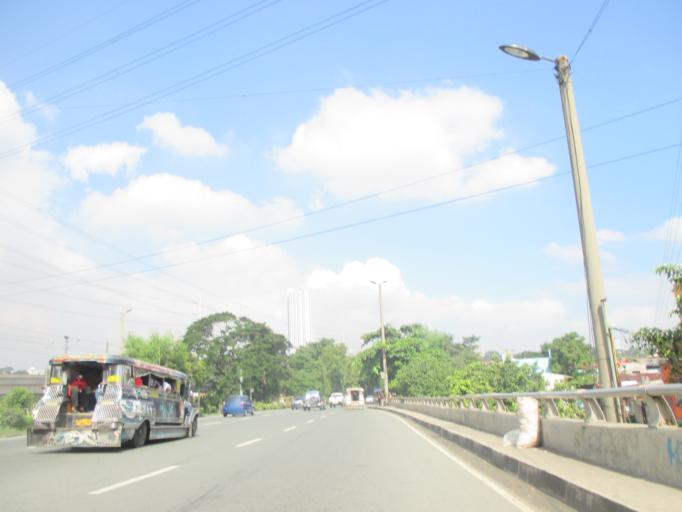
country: PH
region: Metro Manila
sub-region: Marikina
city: Calumpang
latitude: 14.6271
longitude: 121.0818
